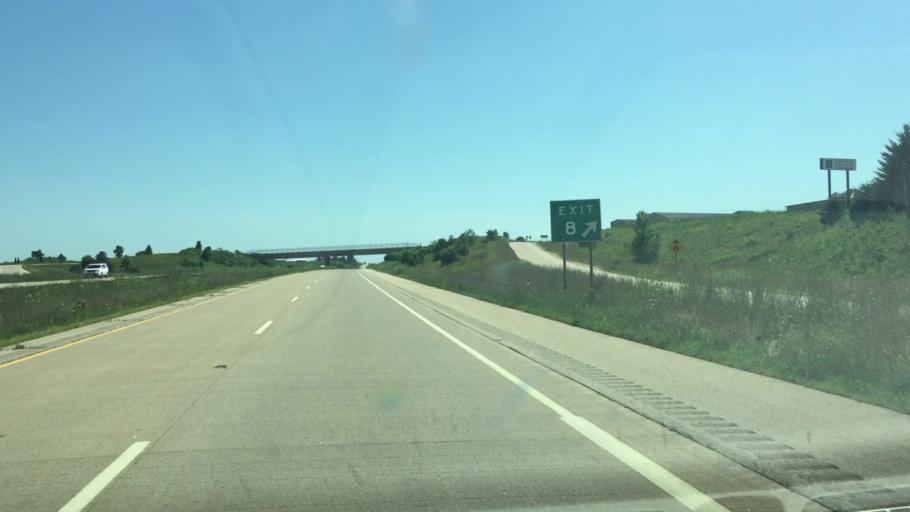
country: US
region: Wisconsin
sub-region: Grant County
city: Dickeyville
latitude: 42.6203
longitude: -90.5846
